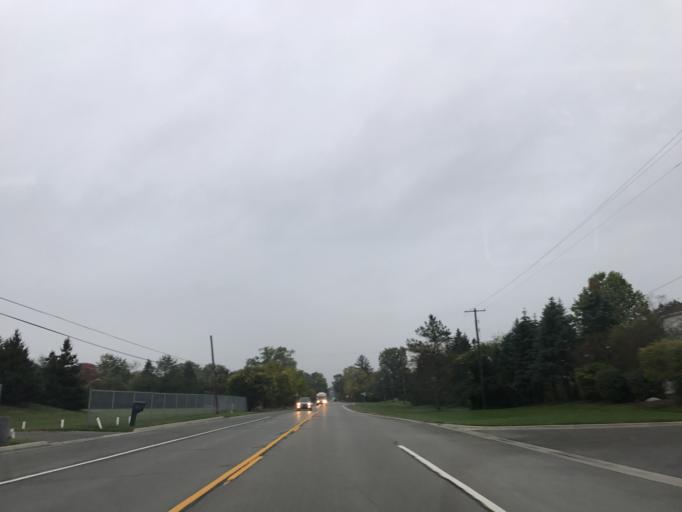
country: US
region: Michigan
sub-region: Oakland County
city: Franklin
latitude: 42.4677
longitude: -83.3181
